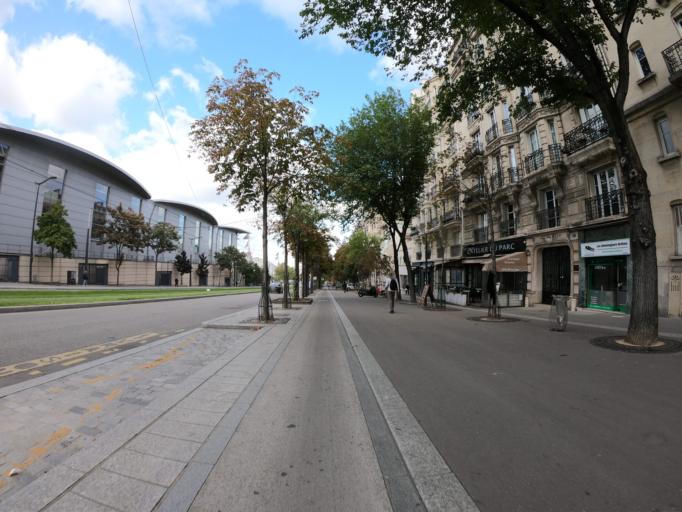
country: FR
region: Ile-de-France
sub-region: Departement des Hauts-de-Seine
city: Vanves
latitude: 48.8316
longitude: 2.2910
